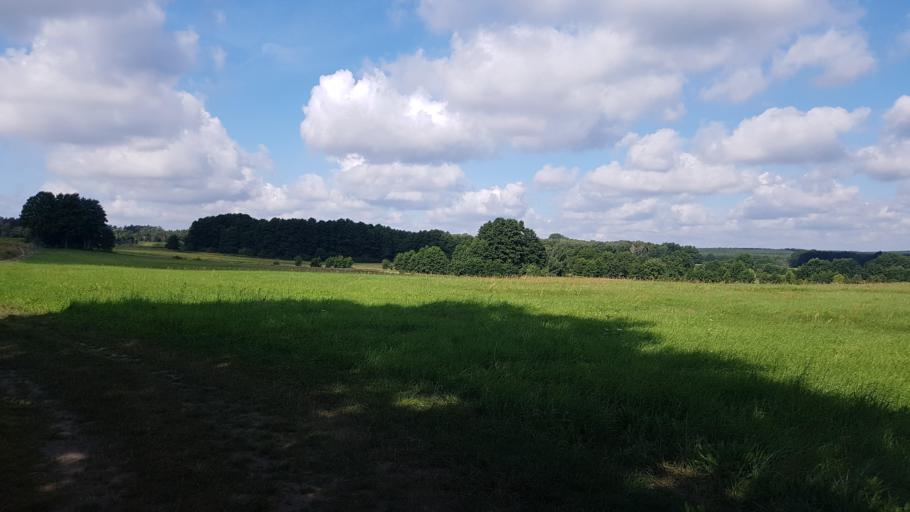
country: DE
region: Brandenburg
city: Sonnewalde
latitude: 51.7471
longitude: 13.6920
